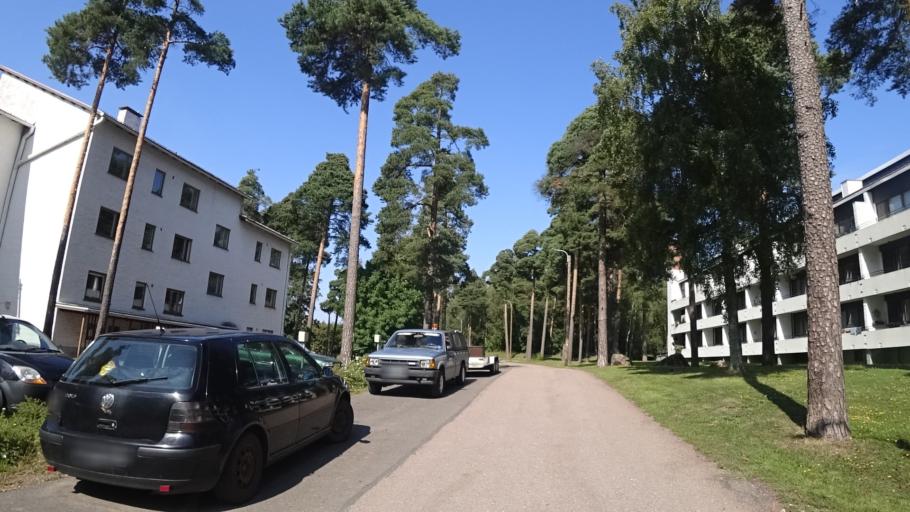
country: FI
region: Kymenlaakso
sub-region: Kotka-Hamina
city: Karhula
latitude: 60.4968
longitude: 26.9585
